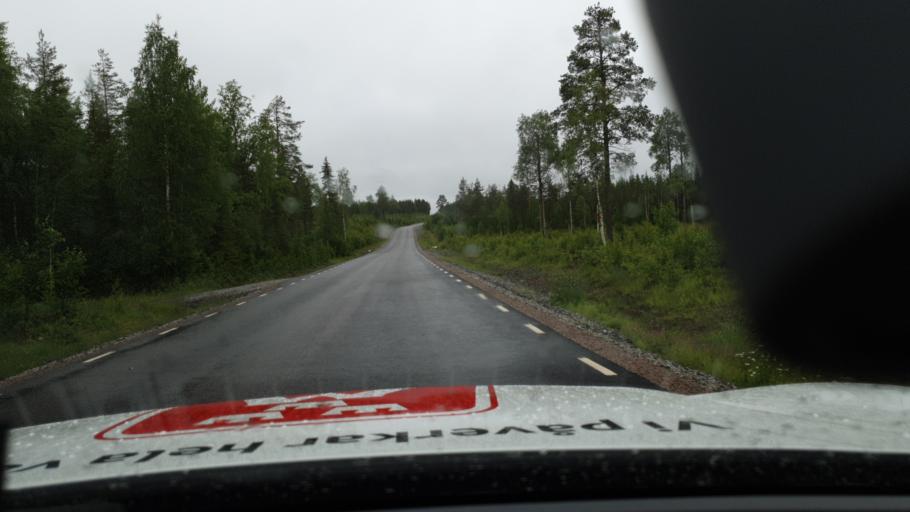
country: SE
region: Norrbotten
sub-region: Overtornea Kommun
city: OEvertornea
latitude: 66.5638
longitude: 23.3334
